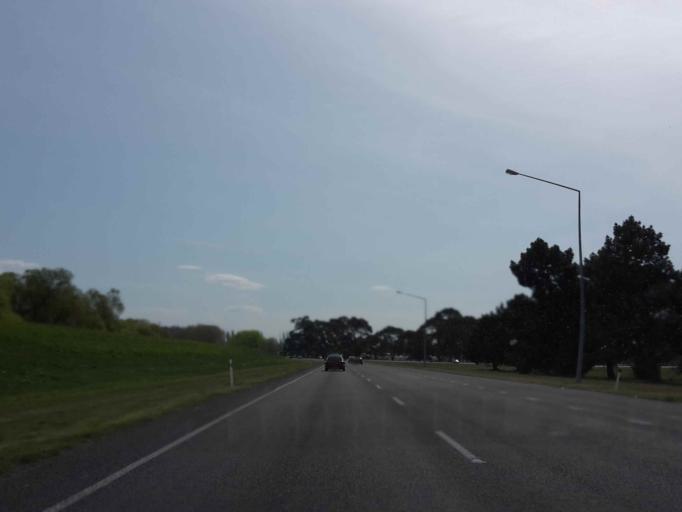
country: NZ
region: Canterbury
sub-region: Waimakariri District
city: Kaiapoi
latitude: -43.4268
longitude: 172.6469
